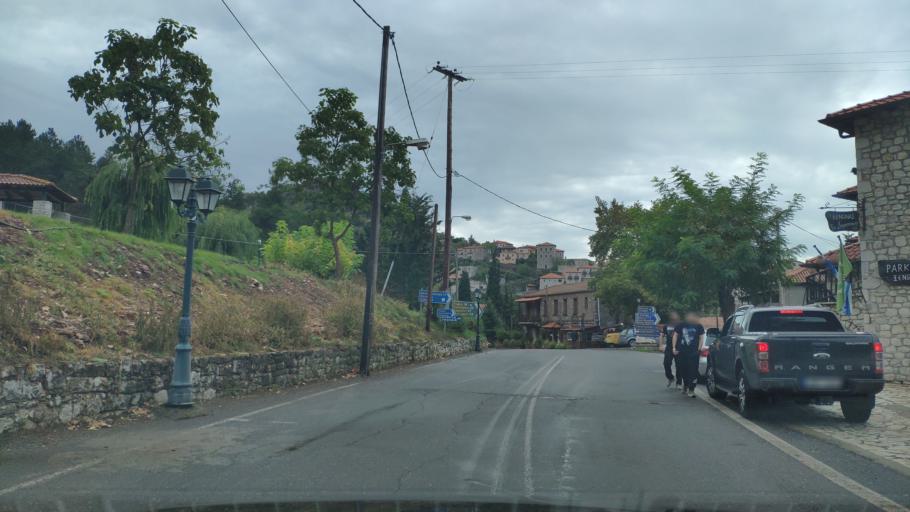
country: GR
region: Peloponnese
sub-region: Nomos Arkadias
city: Dimitsana
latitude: 37.5989
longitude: 22.0409
